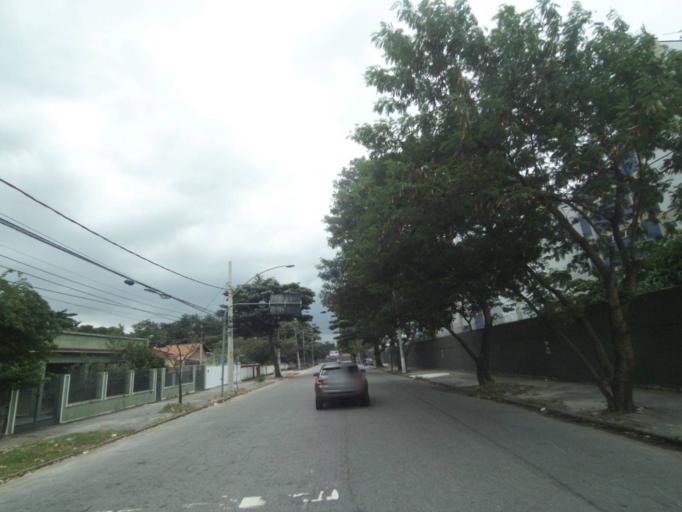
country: BR
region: Rio de Janeiro
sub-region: Nilopolis
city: Nilopolis
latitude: -22.8869
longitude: -43.3901
